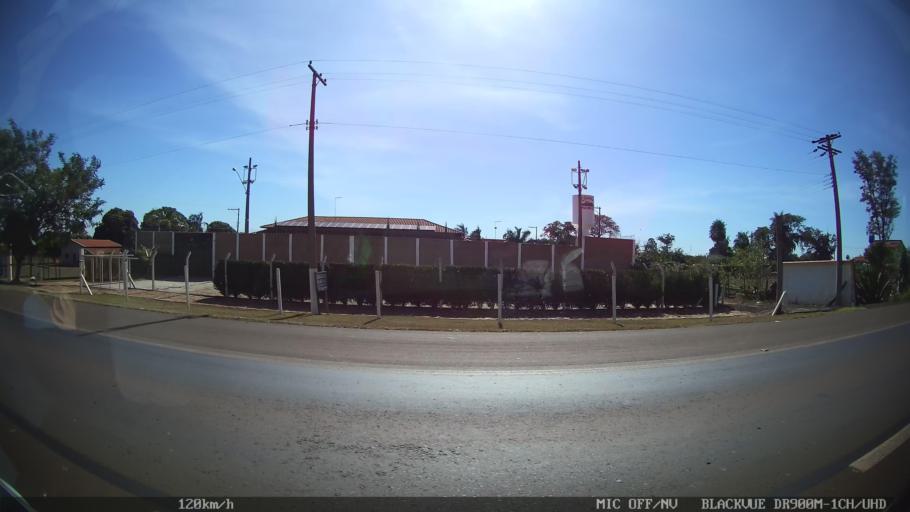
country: BR
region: Sao Paulo
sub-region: Barretos
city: Barretos
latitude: -20.5440
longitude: -48.6214
